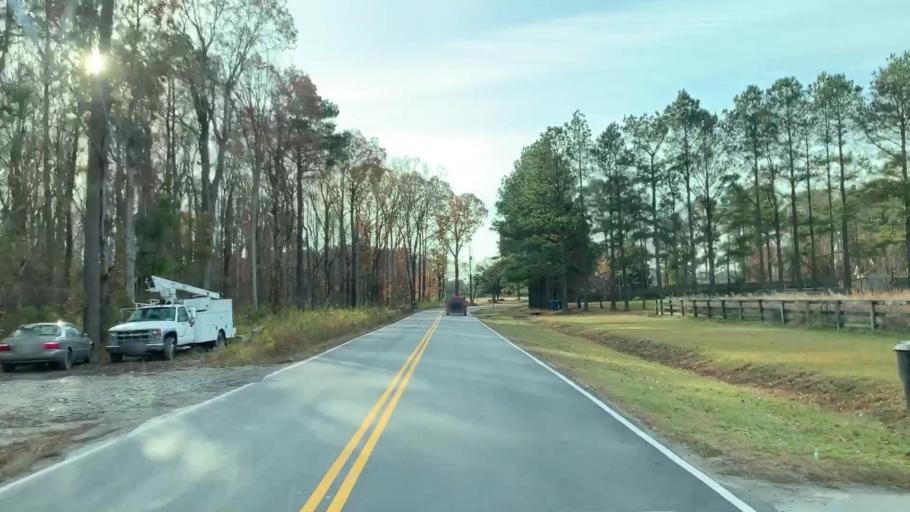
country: US
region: Virginia
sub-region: City of Virginia Beach
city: Virginia Beach
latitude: 36.7120
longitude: -76.0484
